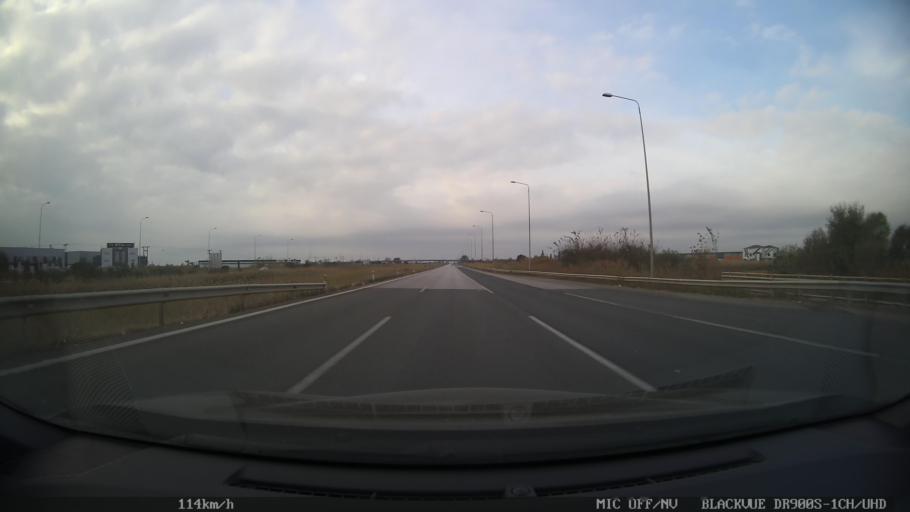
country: GR
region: Central Macedonia
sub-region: Nomos Thessalonikis
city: Sindos
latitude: 40.6496
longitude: 22.8088
